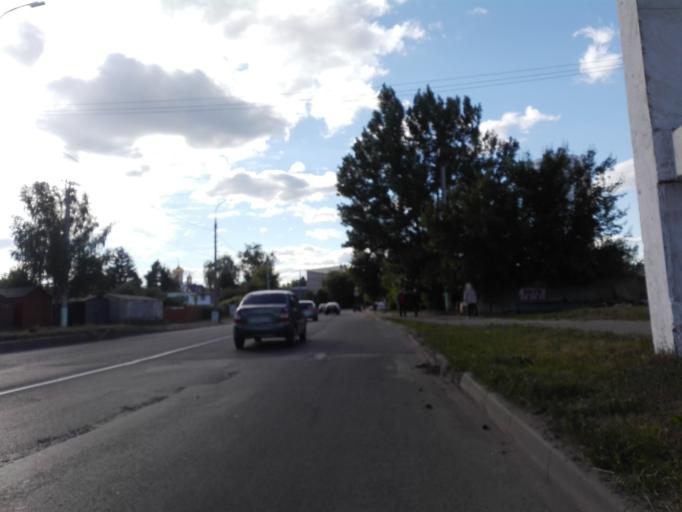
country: RU
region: Orjol
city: Orel
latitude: 52.9511
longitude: 36.0764
